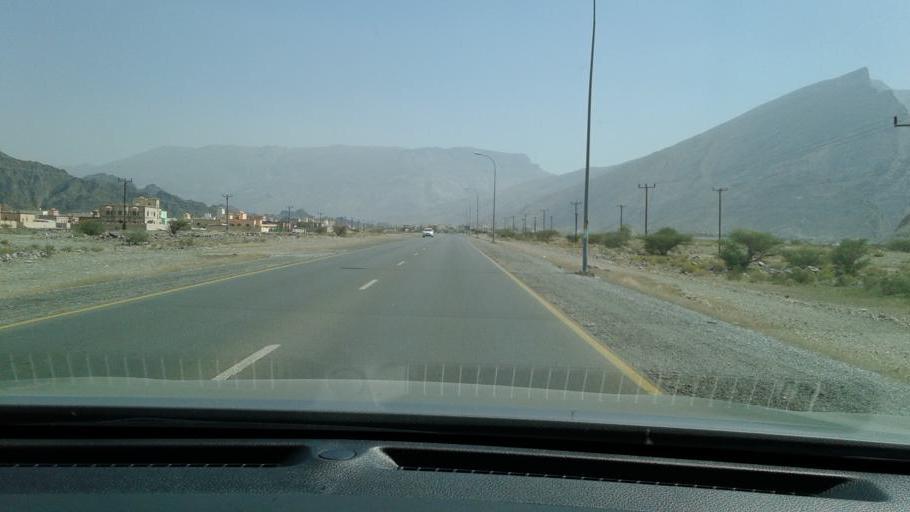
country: OM
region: Al Batinah
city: Bayt al `Awabi
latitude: 23.3506
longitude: 57.4866
